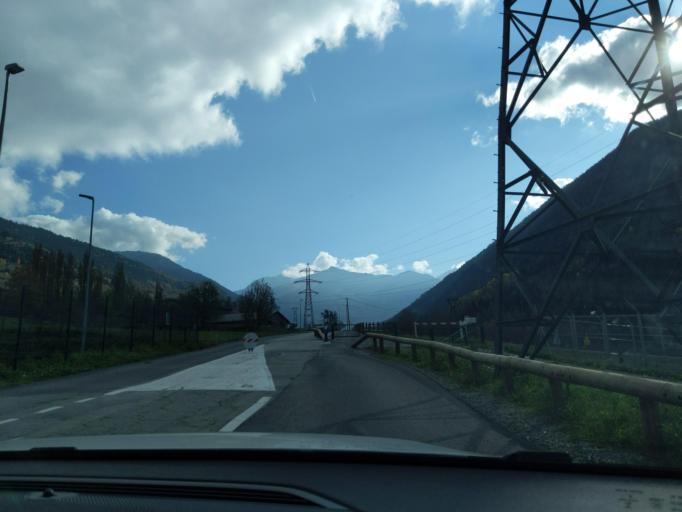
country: FR
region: Rhone-Alpes
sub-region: Departement de la Savoie
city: Seez
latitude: 45.6208
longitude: 6.7929
